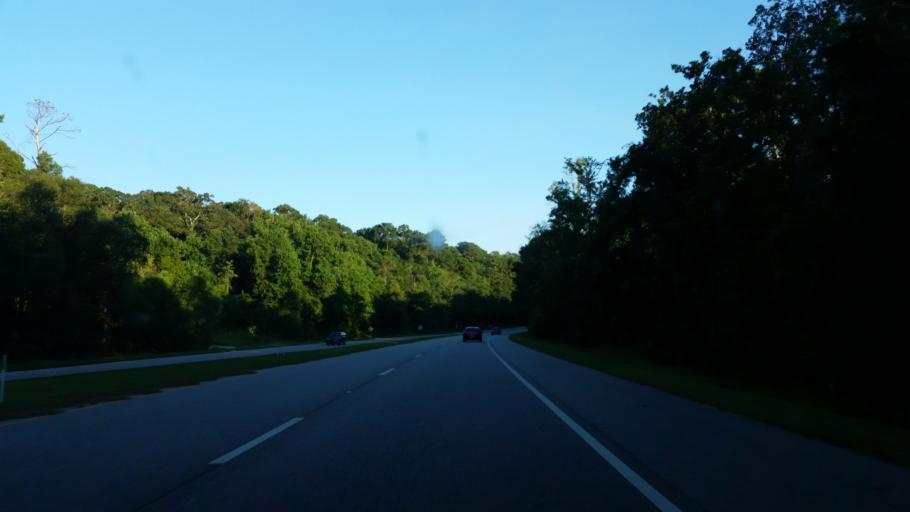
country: US
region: Alabama
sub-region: Baldwin County
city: Spanish Fort
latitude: 30.6645
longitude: -87.9156
